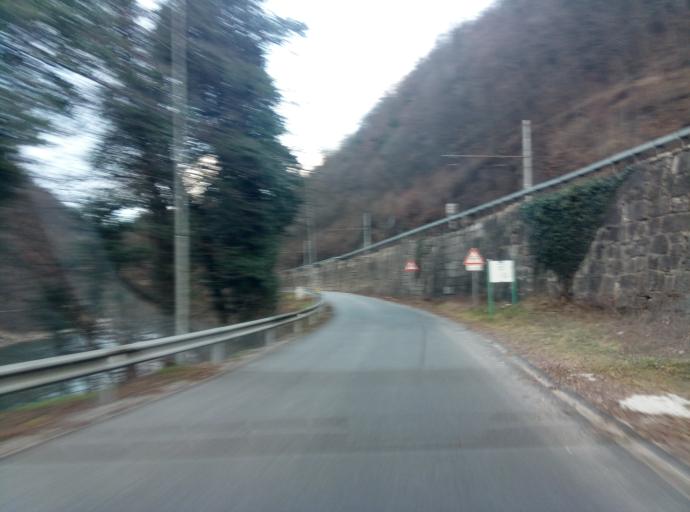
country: SI
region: Hrastnik
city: Dol pri Hrastniku
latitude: 46.1043
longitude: 15.1352
